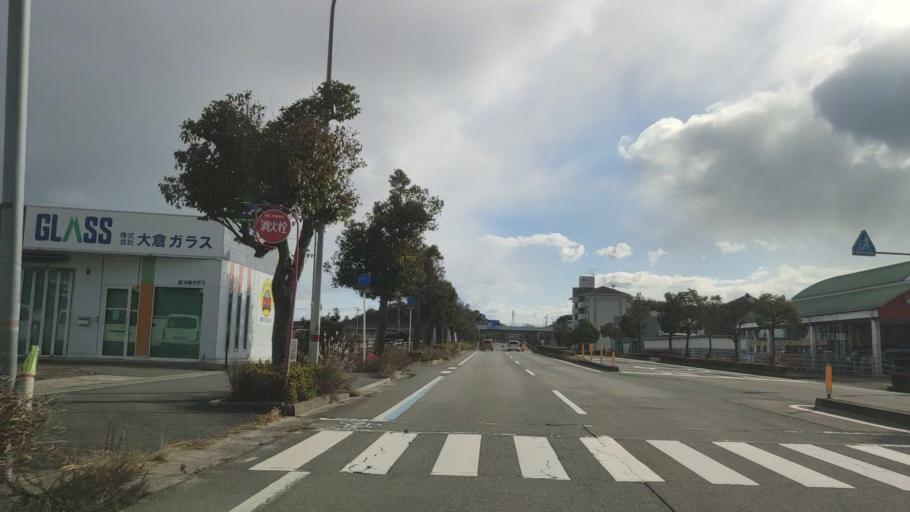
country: JP
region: Ehime
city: Hojo
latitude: 34.0593
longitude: 132.9686
